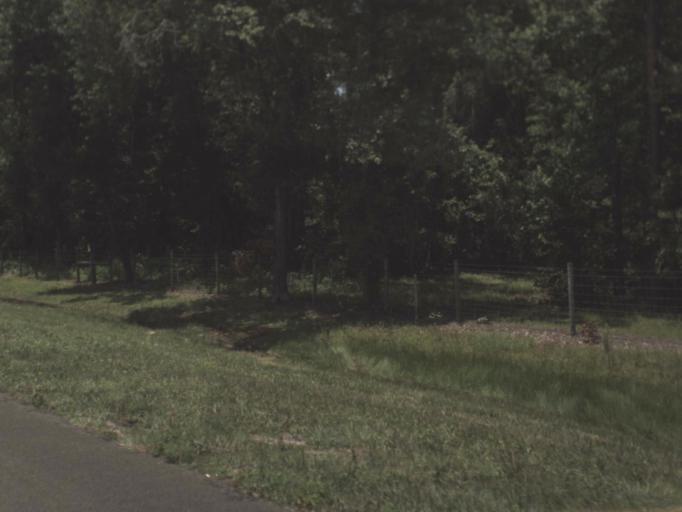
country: US
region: Florida
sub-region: Alachua County
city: Alachua
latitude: 29.8996
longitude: -82.4227
